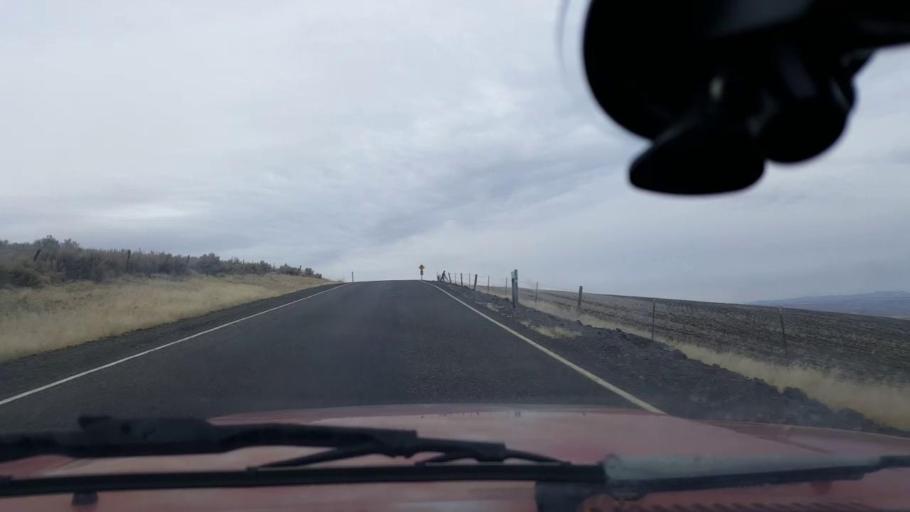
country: US
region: Washington
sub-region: Asotin County
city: Clarkston Heights-Vineland
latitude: 46.3169
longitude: -117.3442
